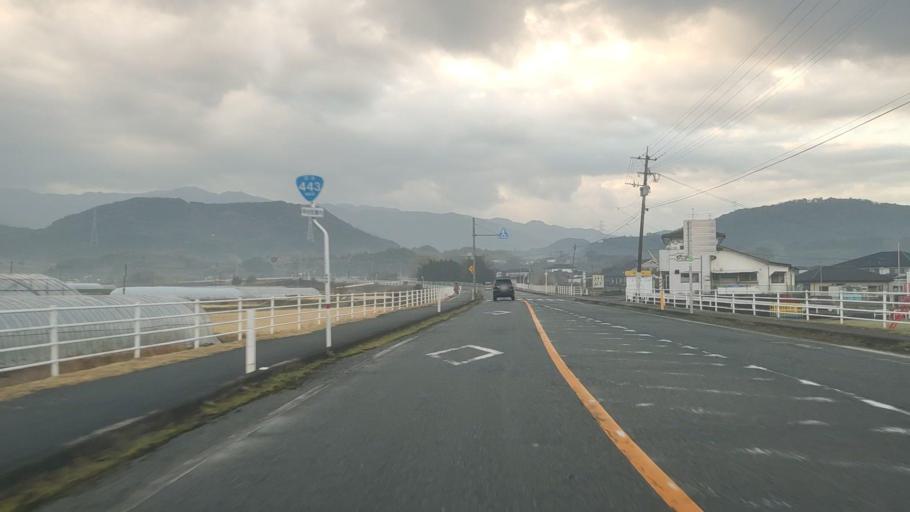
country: JP
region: Kumamoto
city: Matsubase
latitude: 32.6471
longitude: 130.8115
